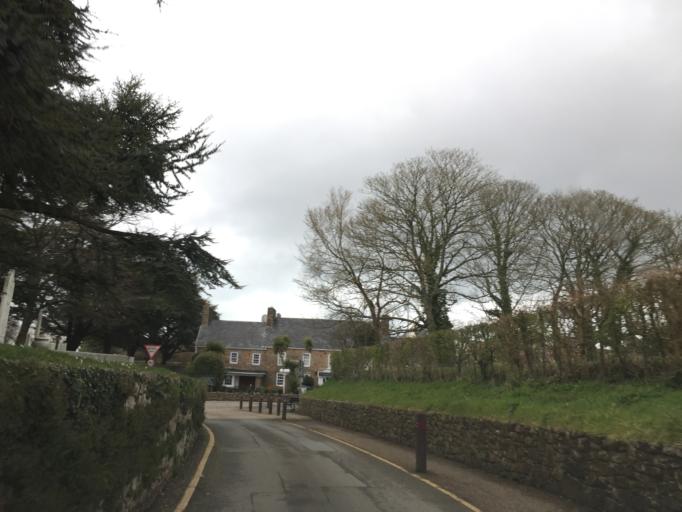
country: JE
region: St Helier
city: Saint Helier
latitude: 49.2347
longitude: -2.1733
